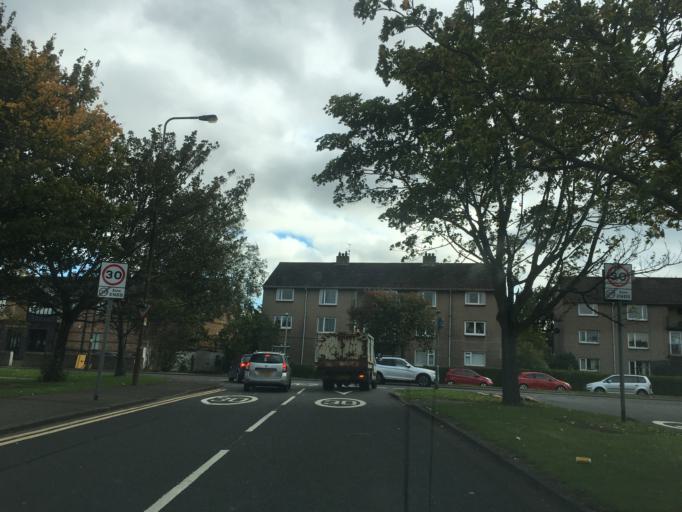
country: GB
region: Scotland
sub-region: Edinburgh
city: Edinburgh
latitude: 55.9675
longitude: -3.2489
